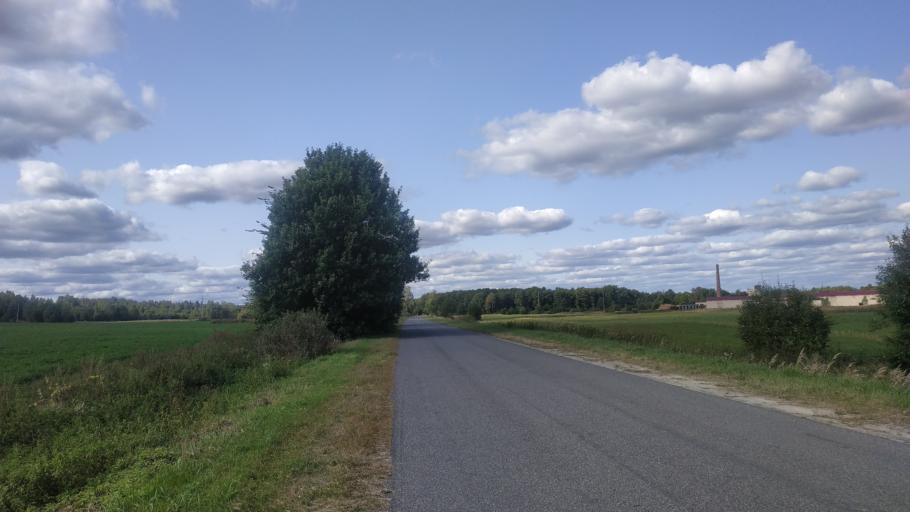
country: RU
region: Brjansk
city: Zhukovka
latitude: 53.4818
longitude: 33.6865
